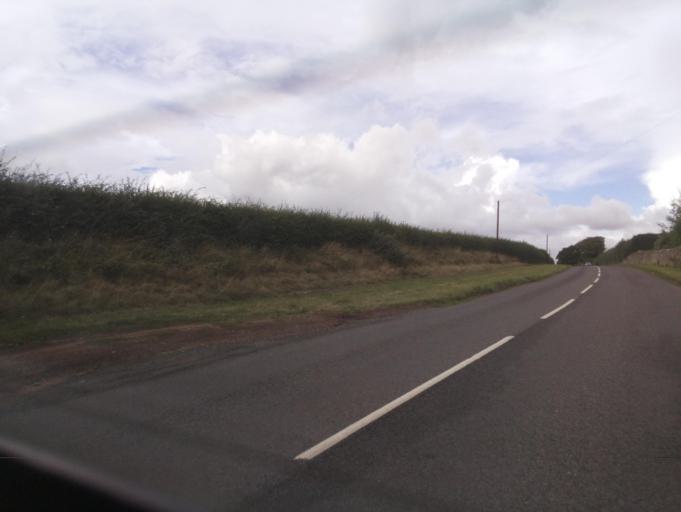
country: GB
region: England
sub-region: Shropshire
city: Woodcote
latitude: 52.7135
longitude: -2.3539
